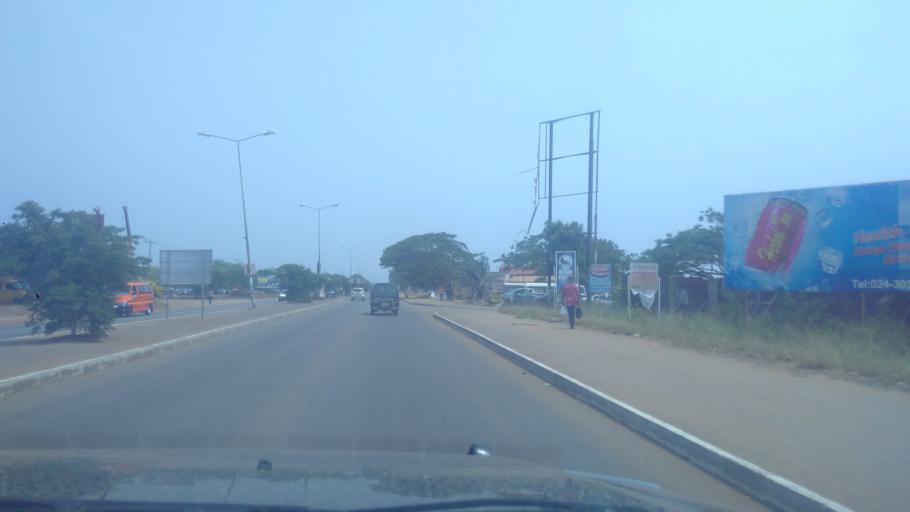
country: GH
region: Greater Accra
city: Tema
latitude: 5.6825
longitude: -0.0136
